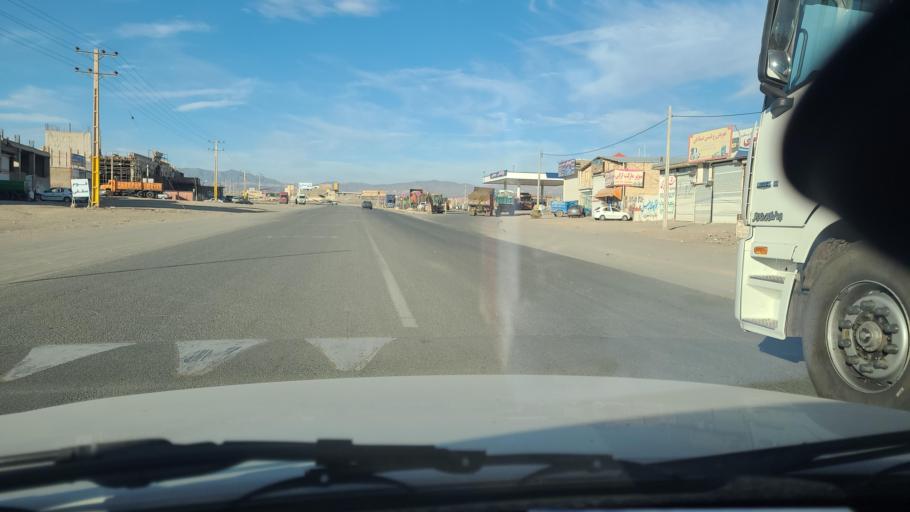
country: IR
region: Razavi Khorasan
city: Sabzevar
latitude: 36.2230
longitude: 57.6517
